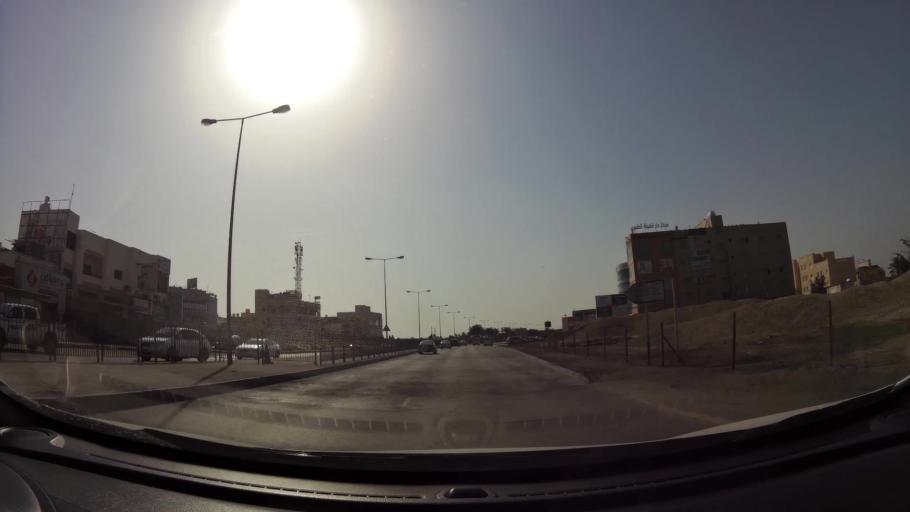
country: BH
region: Manama
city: Jidd Hafs
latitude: 26.2177
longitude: 50.5185
